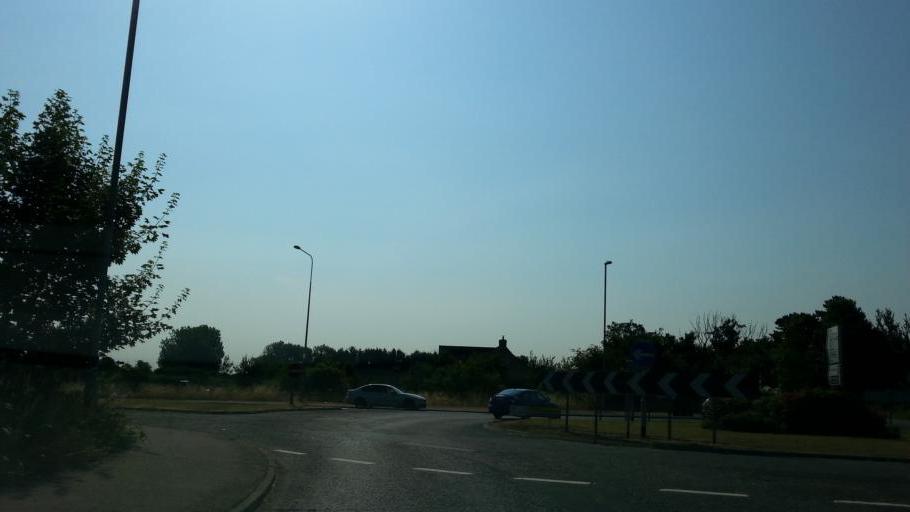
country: GB
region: England
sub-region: Cambridgeshire
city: Brampton
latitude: 52.3270
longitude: -0.2302
